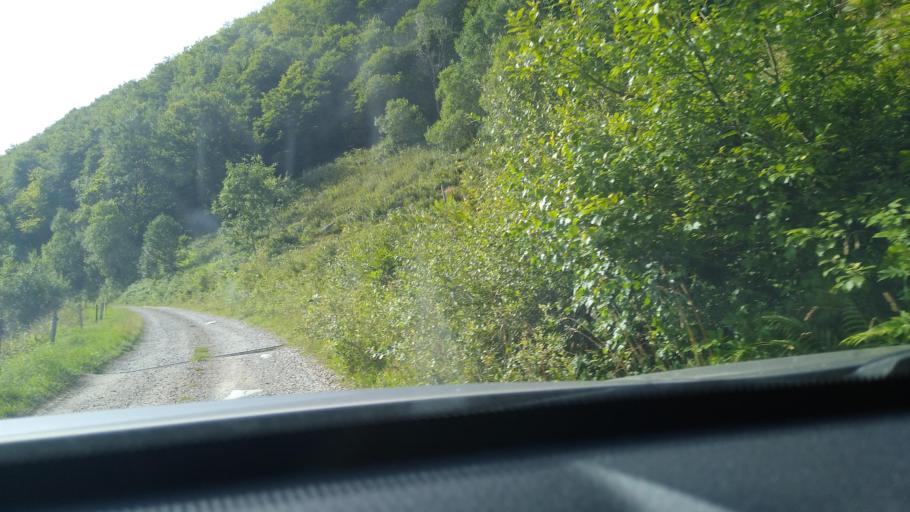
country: FR
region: Midi-Pyrenees
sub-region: Departement de l'Ariege
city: Saint-Girons
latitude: 42.7892
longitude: 1.1450
